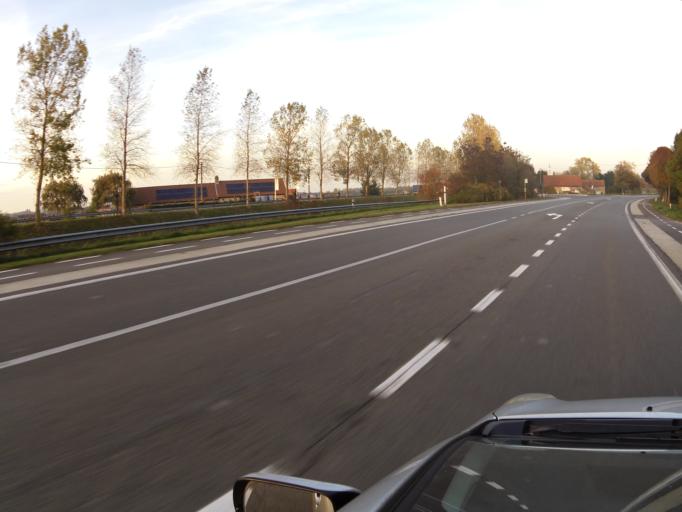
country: BE
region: Flanders
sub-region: Provincie West-Vlaanderen
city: Veurne
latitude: 51.0973
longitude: 2.6827
